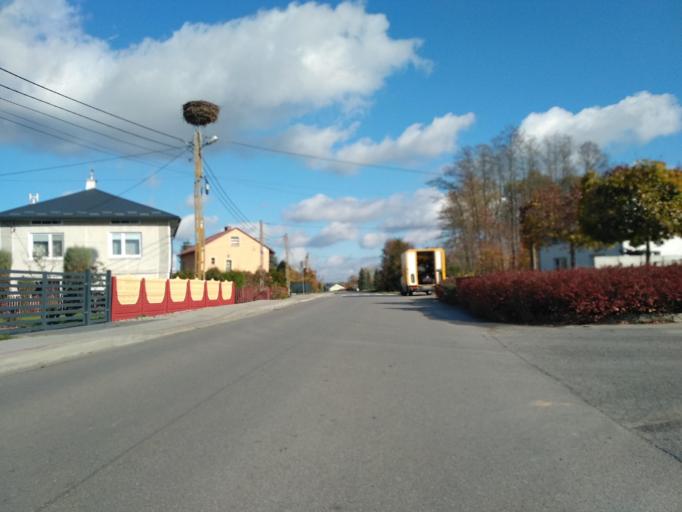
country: PL
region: Subcarpathian Voivodeship
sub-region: Powiat rzeszowski
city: Glogow Malopolski
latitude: 50.1391
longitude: 21.9091
